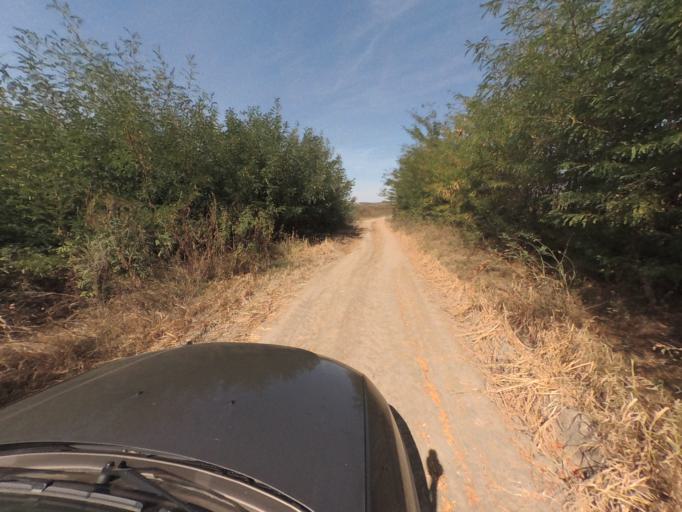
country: RO
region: Vaslui
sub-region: Comuna Costesti
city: Costesti
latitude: 46.5219
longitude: 27.7392
